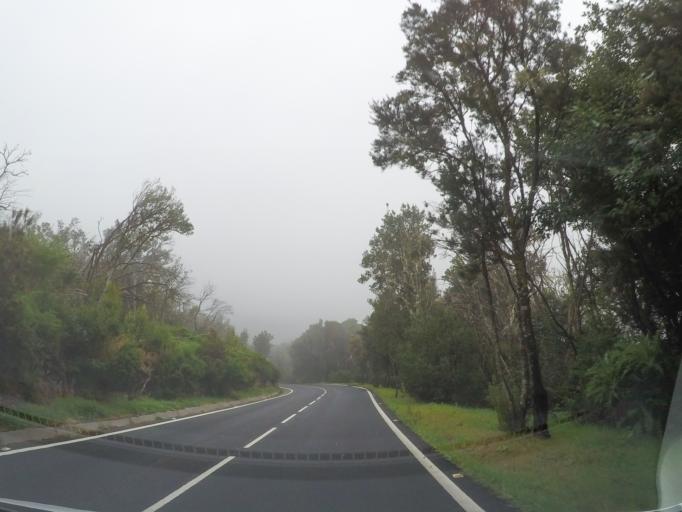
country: ES
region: Canary Islands
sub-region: Provincia de Santa Cruz de Tenerife
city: Vallehermosa
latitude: 28.1316
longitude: -17.2760
